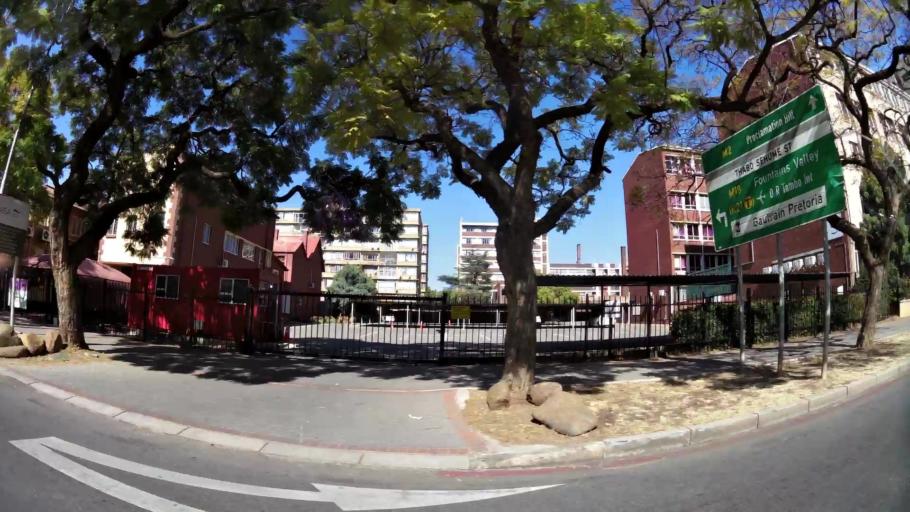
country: ZA
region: Gauteng
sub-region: City of Tshwane Metropolitan Municipality
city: Pretoria
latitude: -25.7506
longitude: 28.1919
